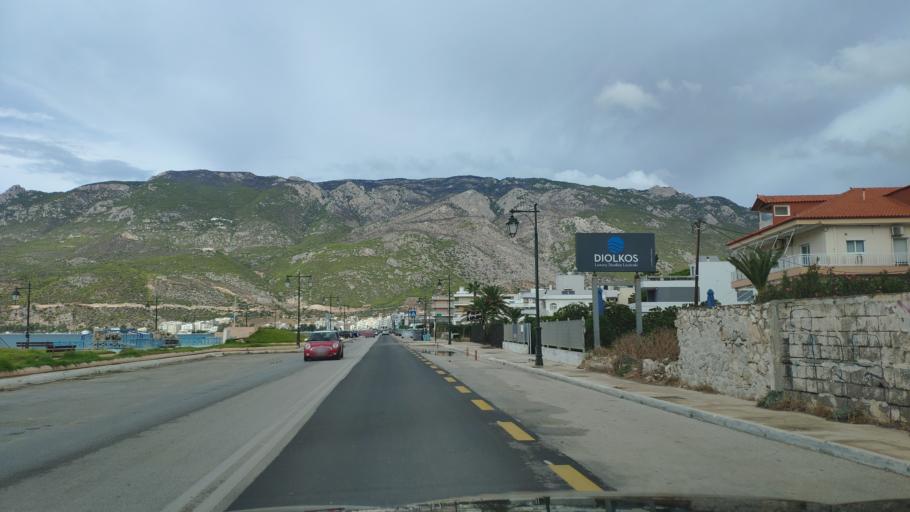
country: GR
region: Peloponnese
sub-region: Nomos Korinthias
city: Loutraki
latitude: 37.9644
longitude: 22.9709
